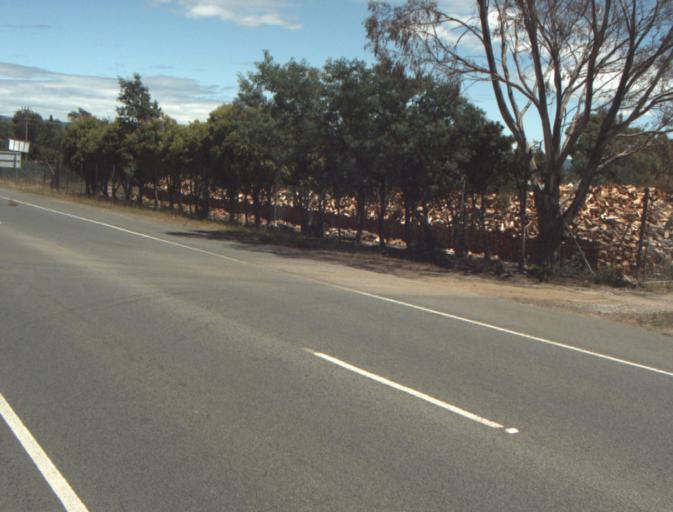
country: AU
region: Tasmania
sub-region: Launceston
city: Mayfield
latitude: -41.3757
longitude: 147.1319
